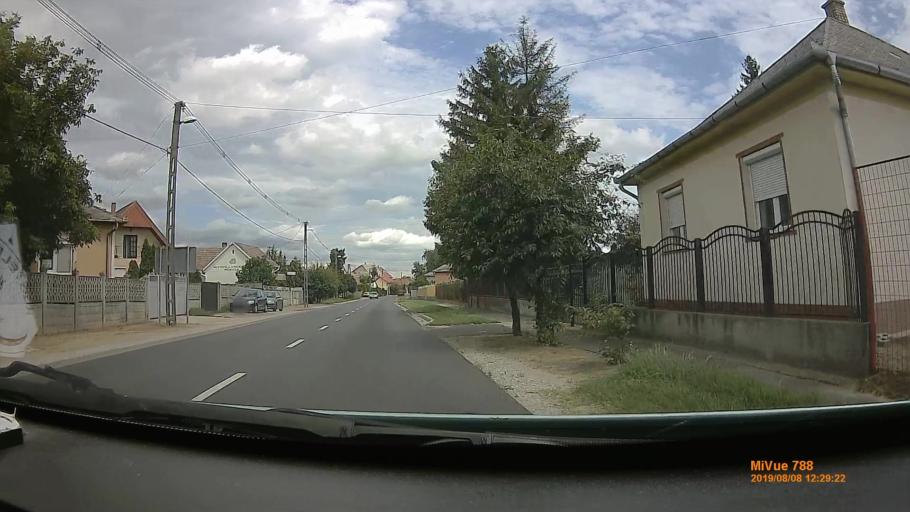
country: HU
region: Szabolcs-Szatmar-Bereg
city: Nyirbator
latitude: 47.8347
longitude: 22.1186
